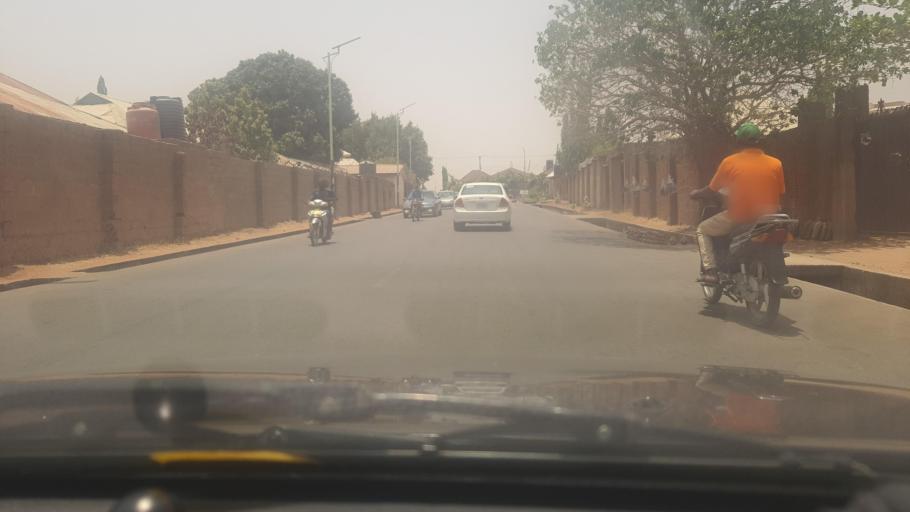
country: NG
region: Gombe
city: Gombe
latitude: 10.2972
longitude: 11.1531
